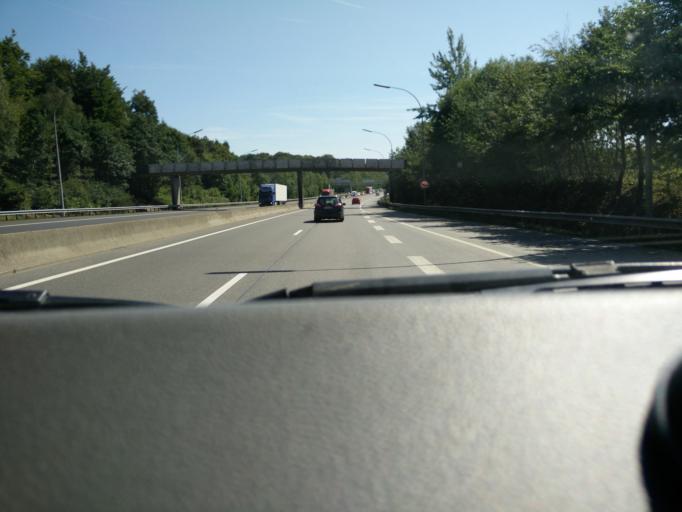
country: LU
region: Luxembourg
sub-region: Canton de Luxembourg
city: Strassen
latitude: 49.6289
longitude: 6.0715
